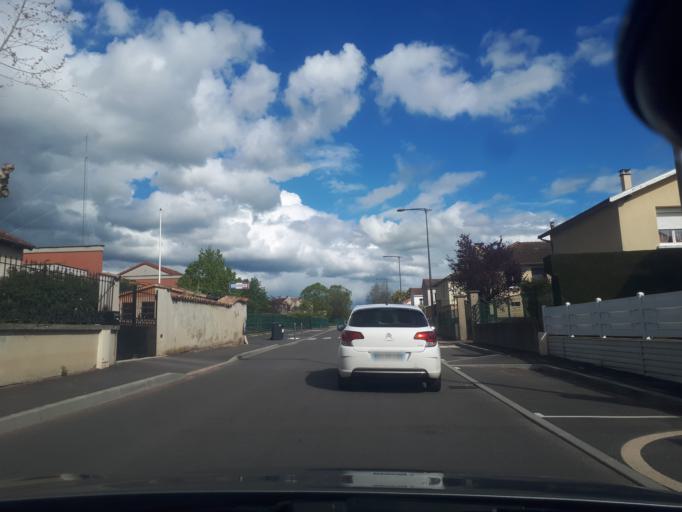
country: FR
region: Rhone-Alpes
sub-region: Departement de la Loire
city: Balbigny
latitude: 45.8182
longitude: 4.1932
